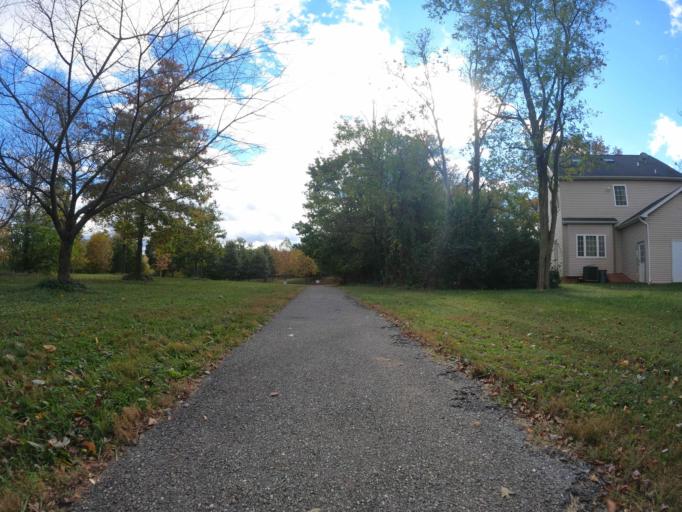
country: US
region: Maryland
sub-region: Carroll County
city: Mount Airy
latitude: 39.3778
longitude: -77.1491
